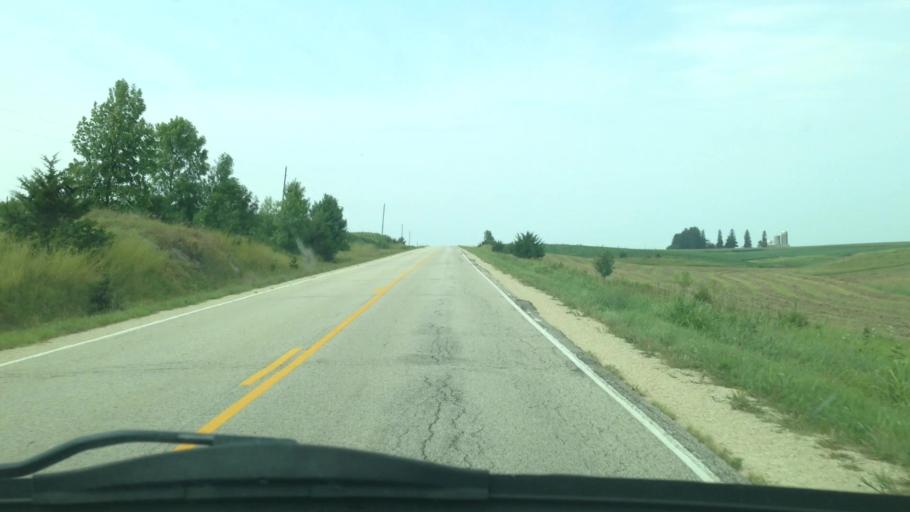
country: US
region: Minnesota
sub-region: Winona County
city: Saint Charles
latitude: 43.8530
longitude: -91.9594
